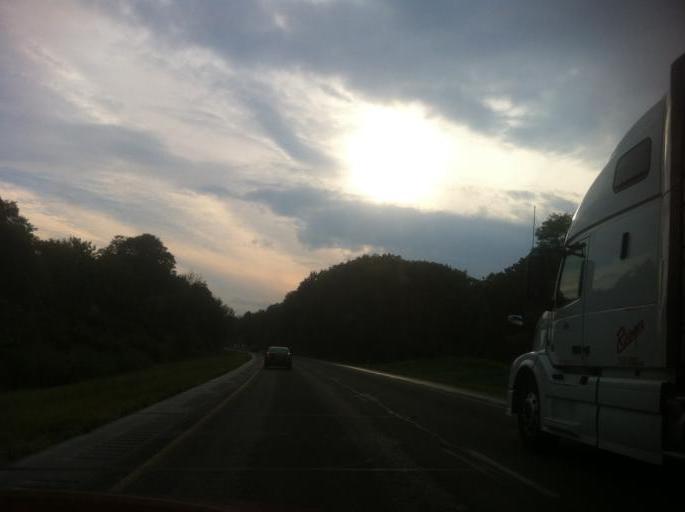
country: US
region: Pennsylvania
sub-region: Clarion County
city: Knox
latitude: 41.1954
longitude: -79.5797
